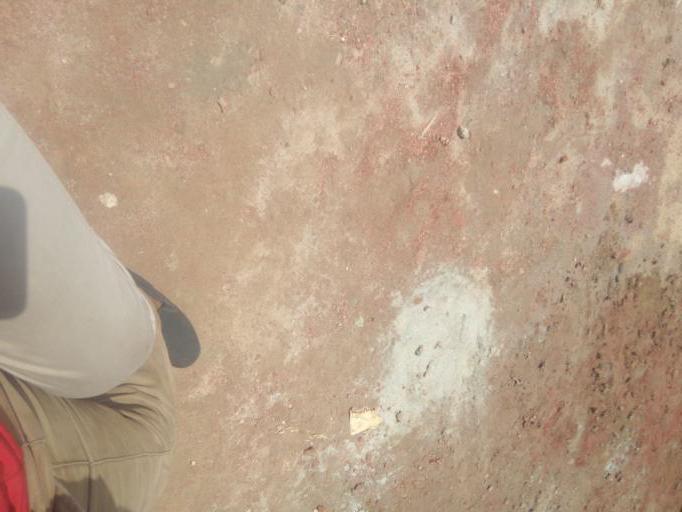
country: BD
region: Dhaka
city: Azimpur
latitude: 23.7522
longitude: 90.3520
